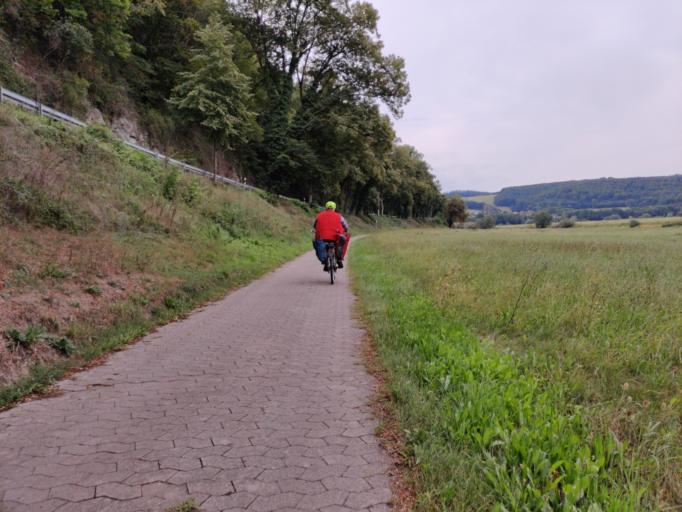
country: DE
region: Lower Saxony
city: Pegestorf
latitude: 51.9111
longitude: 9.4680
